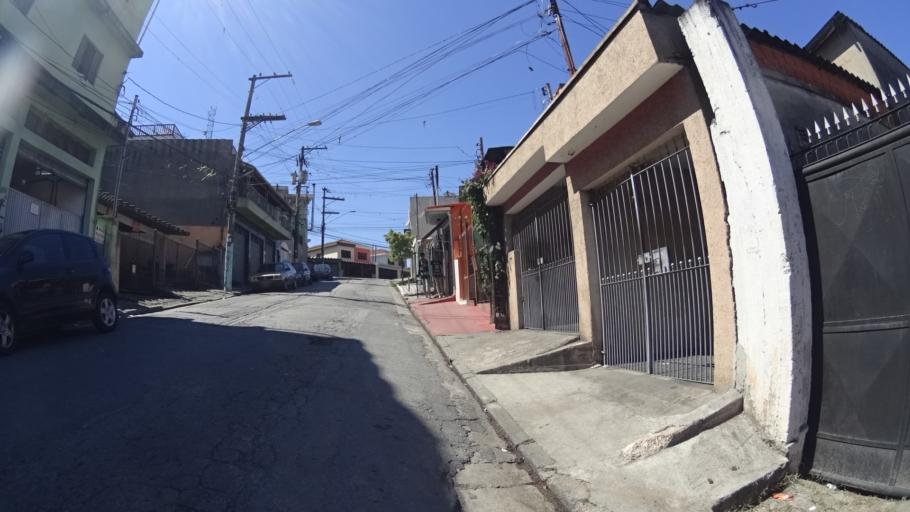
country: BR
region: Sao Paulo
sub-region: Sao Paulo
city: Sao Paulo
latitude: -23.4839
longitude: -46.6702
